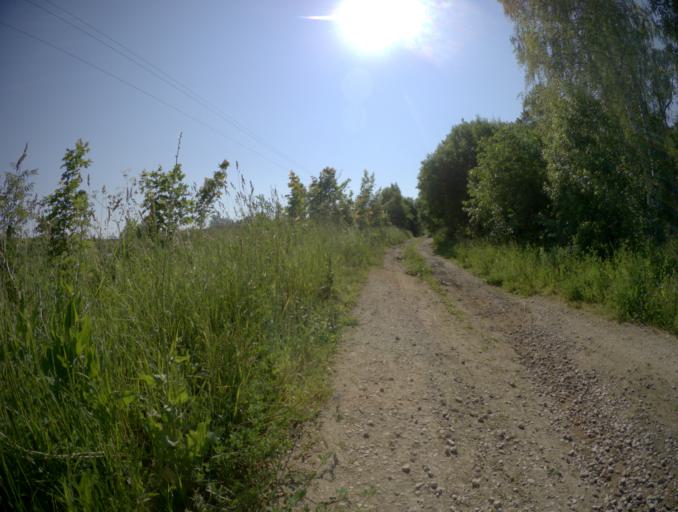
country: RU
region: Vladimir
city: Novovyazniki
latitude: 56.1943
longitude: 42.2454
